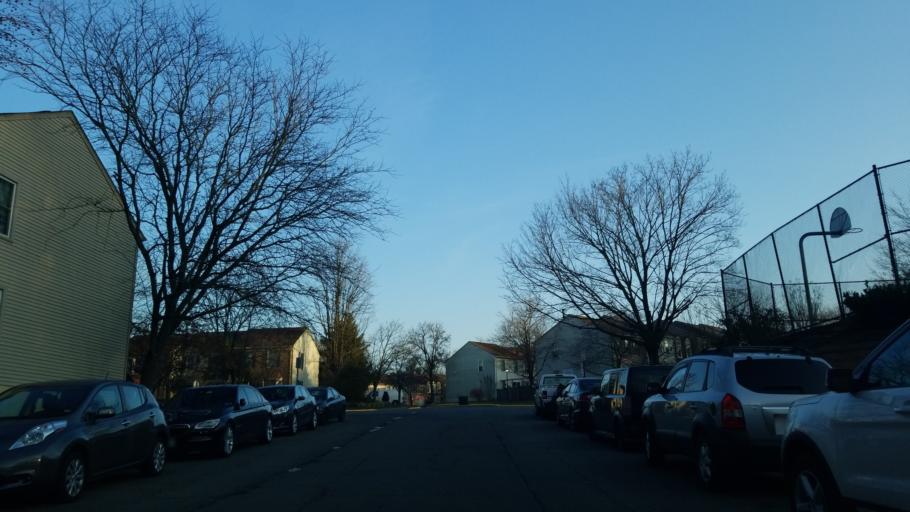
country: US
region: Virginia
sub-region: Fairfax County
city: Centreville
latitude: 38.8465
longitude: -77.4393
